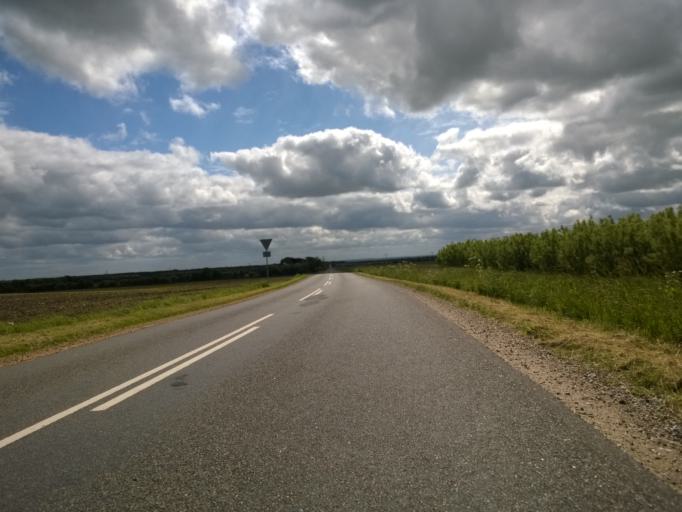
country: DK
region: Central Jutland
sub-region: Holstebro Kommune
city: Vinderup
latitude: 56.4252
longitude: 8.8463
